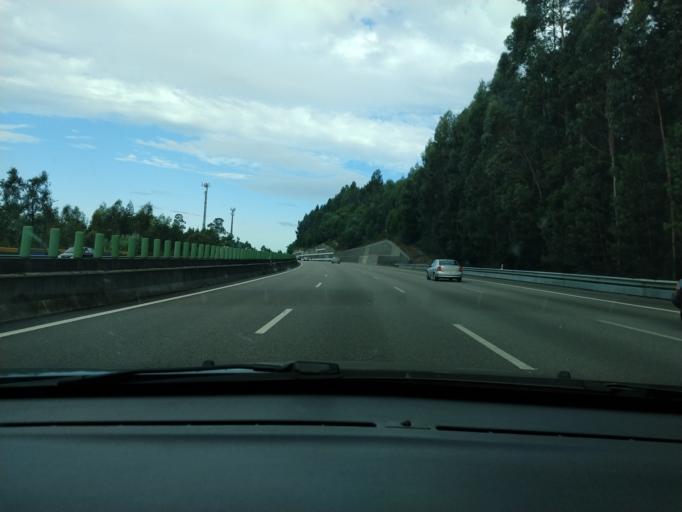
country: PT
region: Porto
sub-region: Vila Nova de Gaia
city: Perozinho
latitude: 41.0515
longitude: -8.5727
